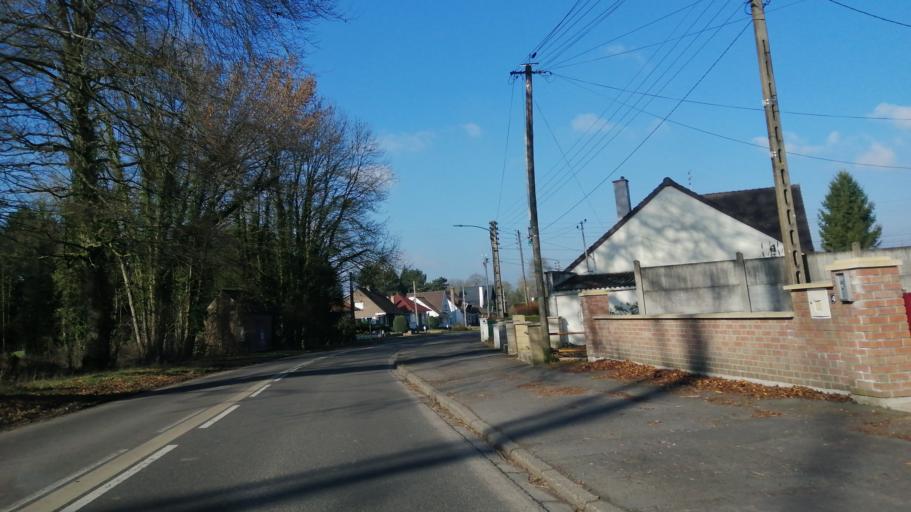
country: FR
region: Nord-Pas-de-Calais
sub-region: Departement du Pas-de-Calais
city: Ranchicourt
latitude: 50.4447
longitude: 2.5496
